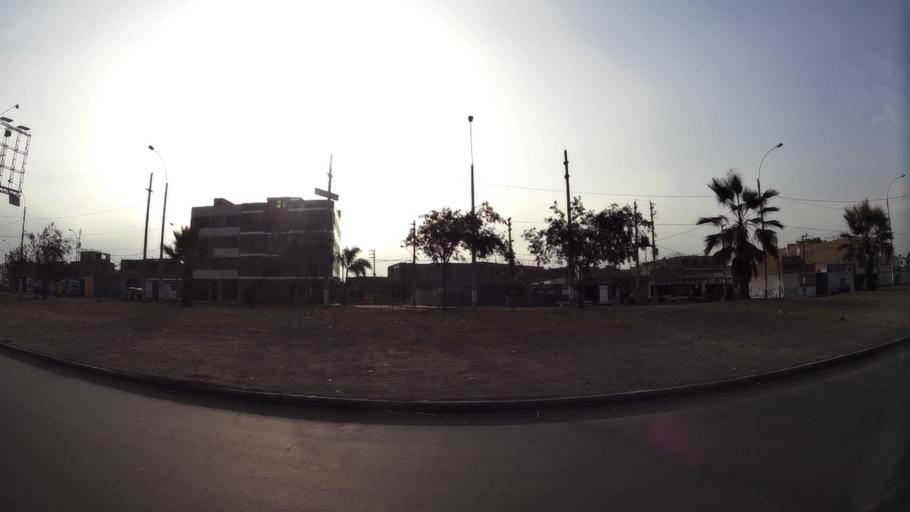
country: PE
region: Lima
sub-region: Lima
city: Independencia
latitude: -11.9885
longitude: -77.1045
